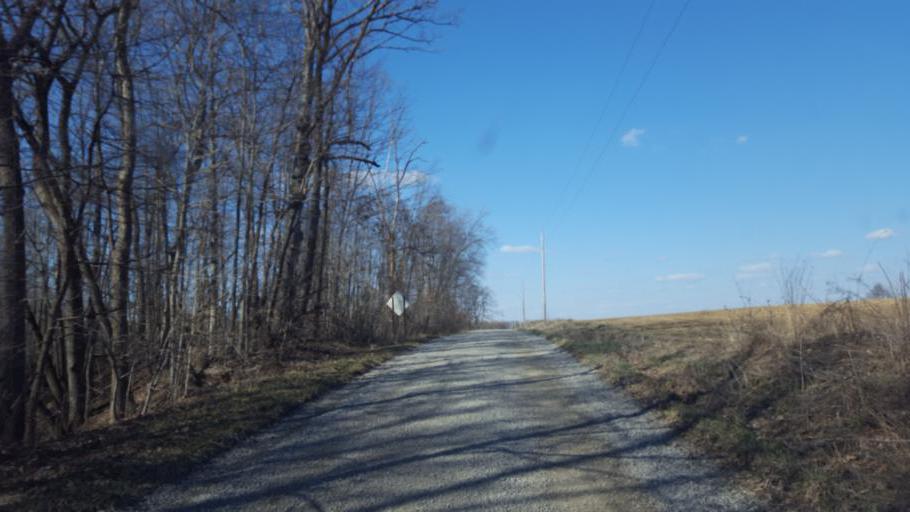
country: US
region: Ohio
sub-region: Morrow County
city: Mount Gilead
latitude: 40.4645
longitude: -82.7449
